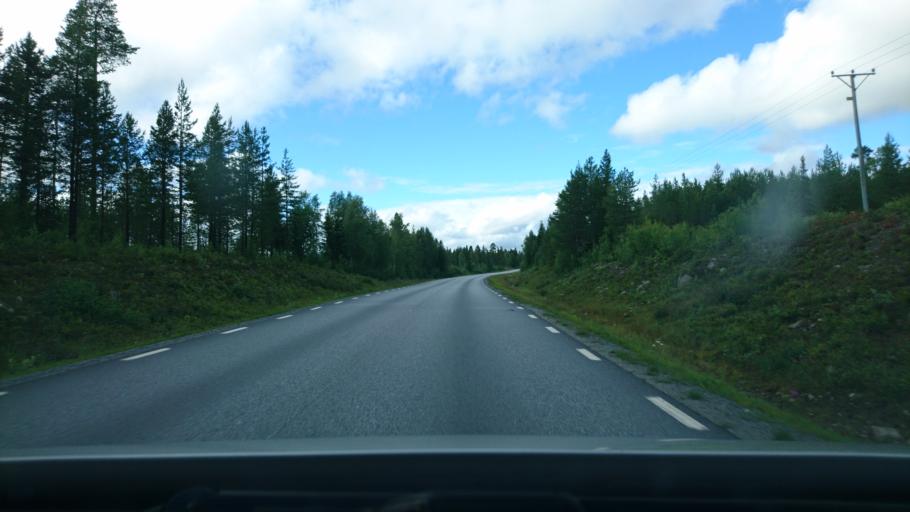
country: SE
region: Vaesterbotten
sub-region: Vilhelmina Kommun
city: Vilhelmina
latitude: 64.5489
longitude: 16.7426
